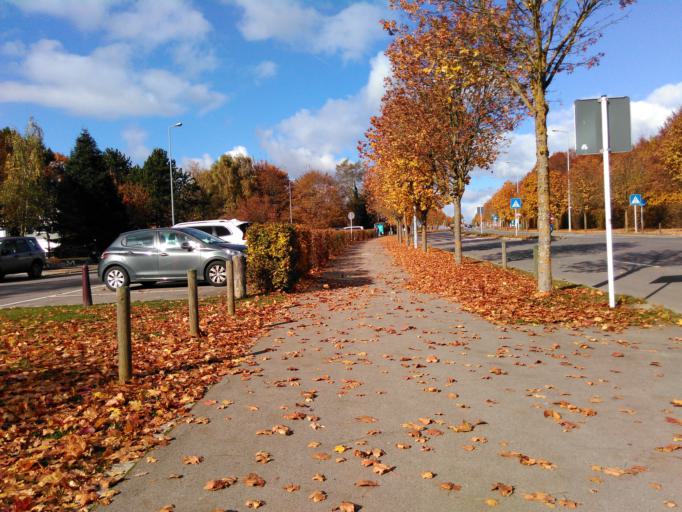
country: LU
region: Luxembourg
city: Kirchberg
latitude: 49.6270
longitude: 6.1603
